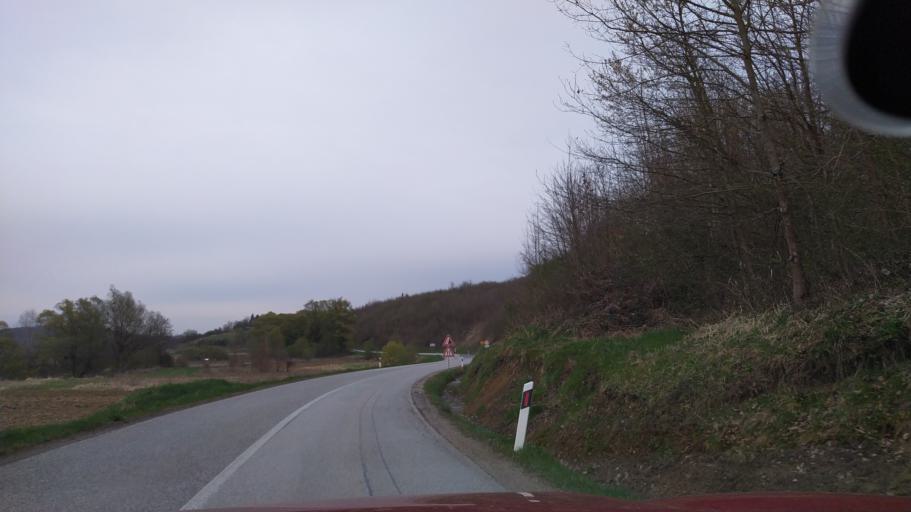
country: HR
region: Varazdinska
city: Jalzabet
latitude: 46.2116
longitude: 16.4998
